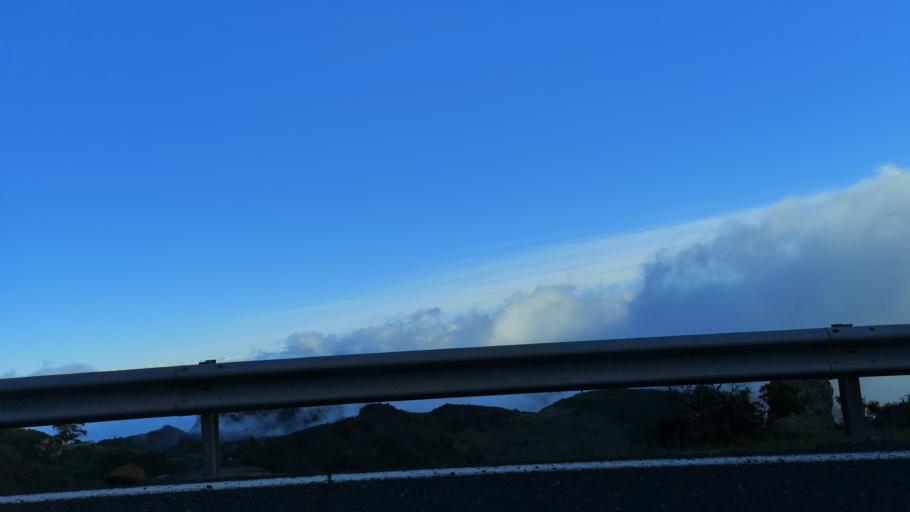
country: ES
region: Canary Islands
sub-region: Provincia de Santa Cruz de Tenerife
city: Alajero
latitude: 28.0897
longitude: -17.2543
